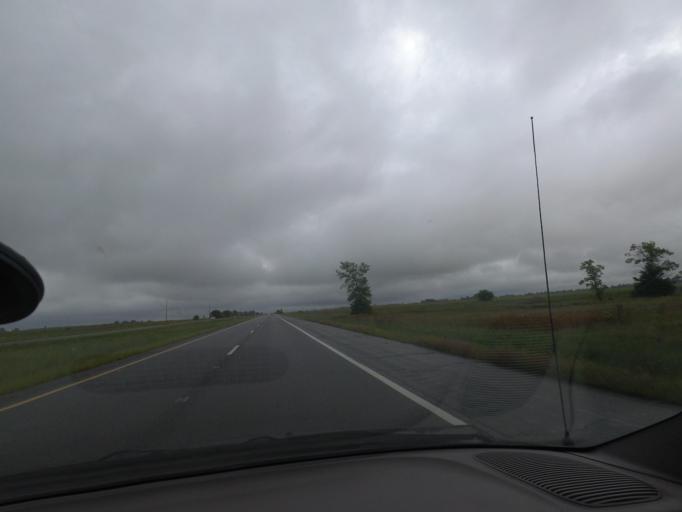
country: US
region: Illinois
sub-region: Champaign County
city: Mahomet
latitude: 40.1203
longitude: -88.4068
